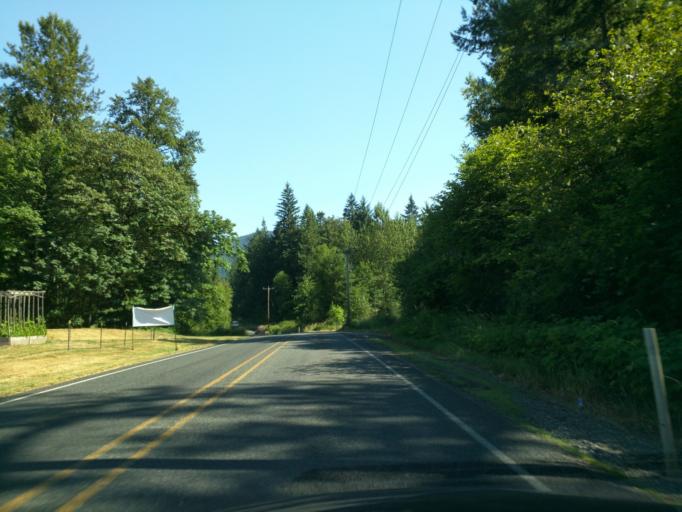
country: US
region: Washington
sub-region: Whatcom County
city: Peaceful Valley
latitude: 48.8007
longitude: -122.1955
